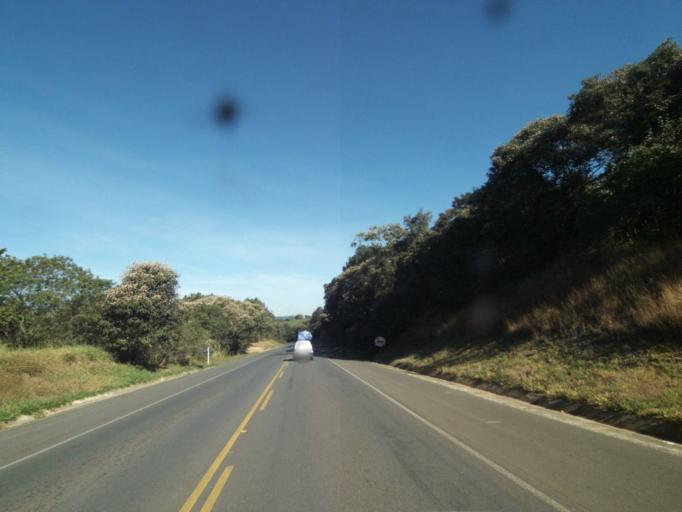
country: BR
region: Parana
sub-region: Tibagi
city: Tibagi
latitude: -24.5070
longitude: -50.4415
